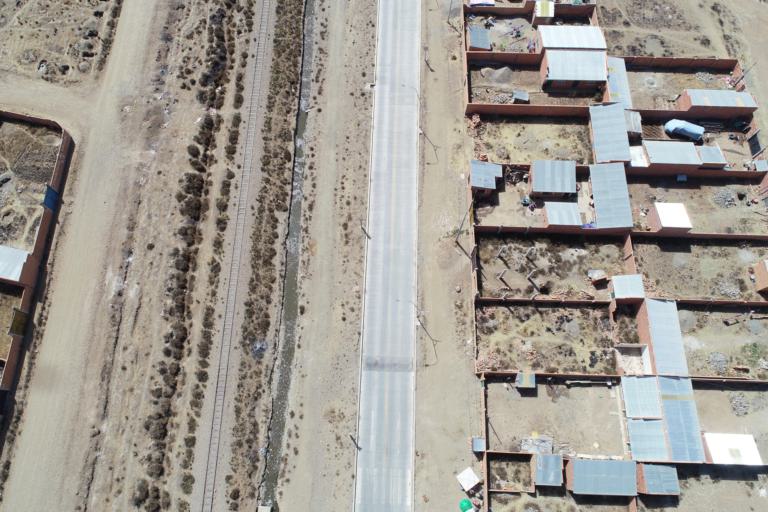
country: BO
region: La Paz
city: La Paz
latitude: -16.5927
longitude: -68.2148
